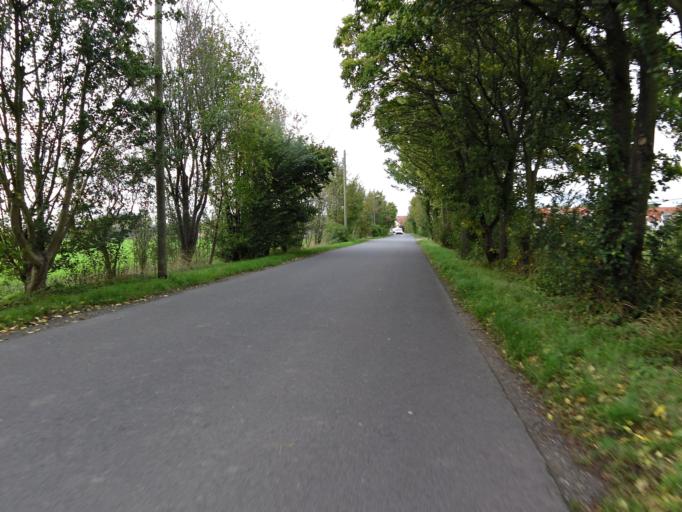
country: DE
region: Saxony
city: Grossposna
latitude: 51.2993
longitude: 12.4458
